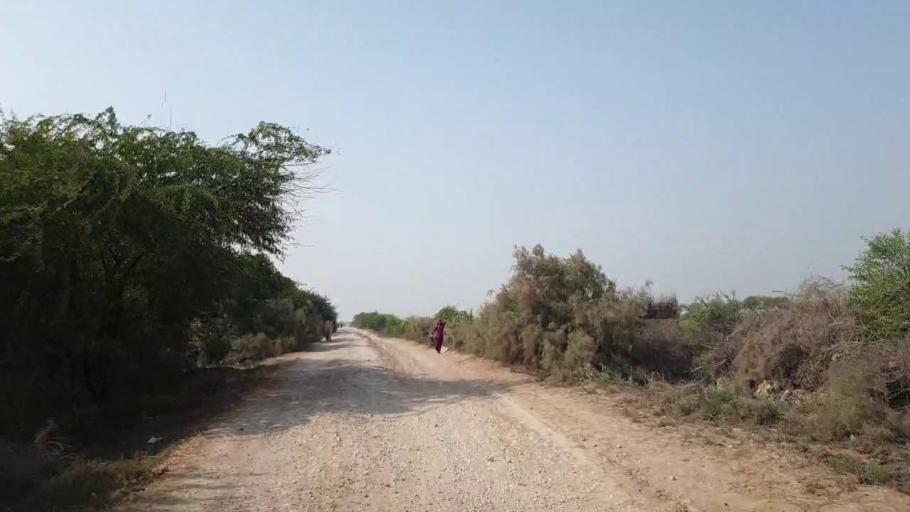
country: PK
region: Sindh
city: Kario
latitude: 24.9356
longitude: 68.5526
